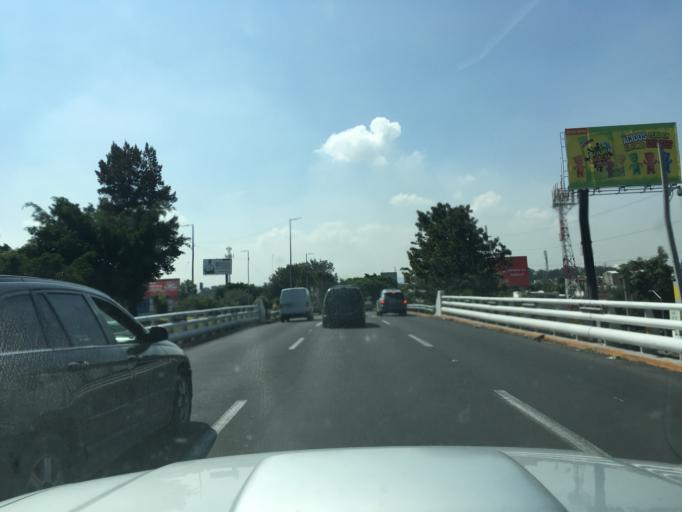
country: MX
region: Jalisco
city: Guadalajara
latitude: 20.6532
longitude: -103.3724
